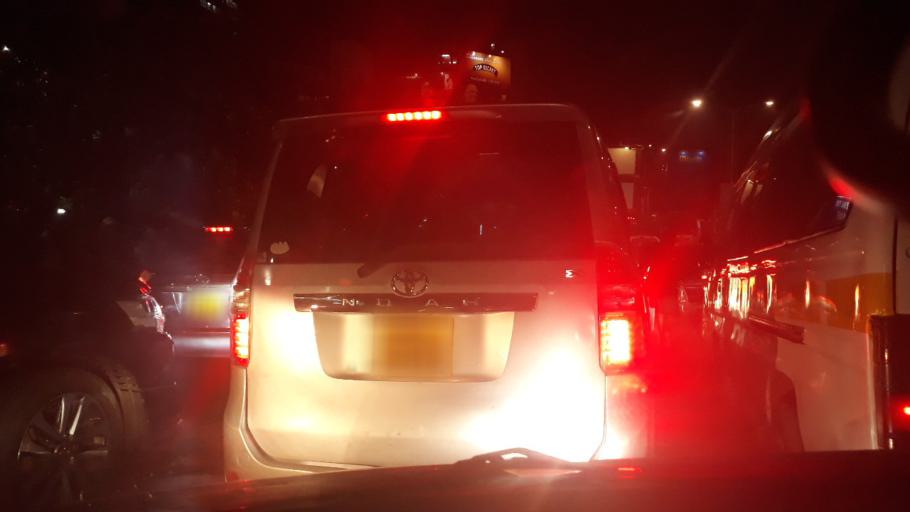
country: KE
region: Nairobi Area
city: Nairobi
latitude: -1.2895
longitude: 36.8269
